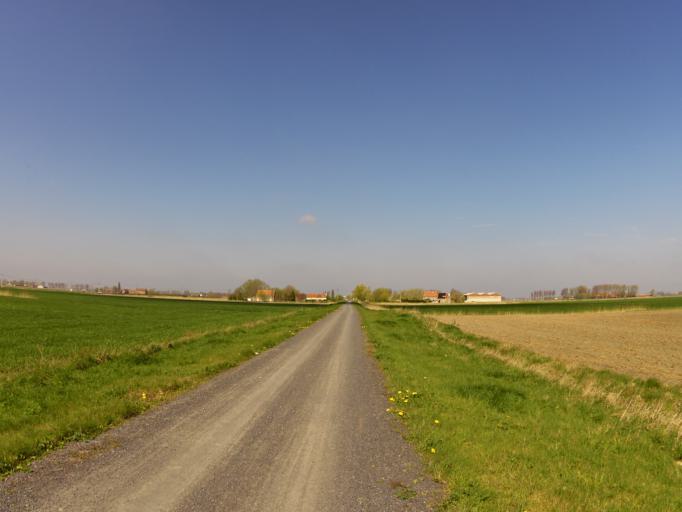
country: BE
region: Flanders
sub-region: Provincie West-Vlaanderen
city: Nieuwpoort
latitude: 51.0891
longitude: 2.7860
